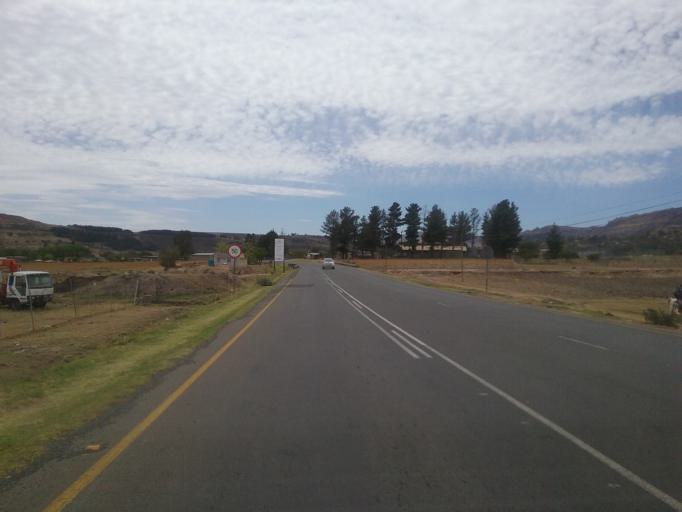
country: LS
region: Maseru
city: Nako
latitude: -29.6245
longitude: 27.4930
